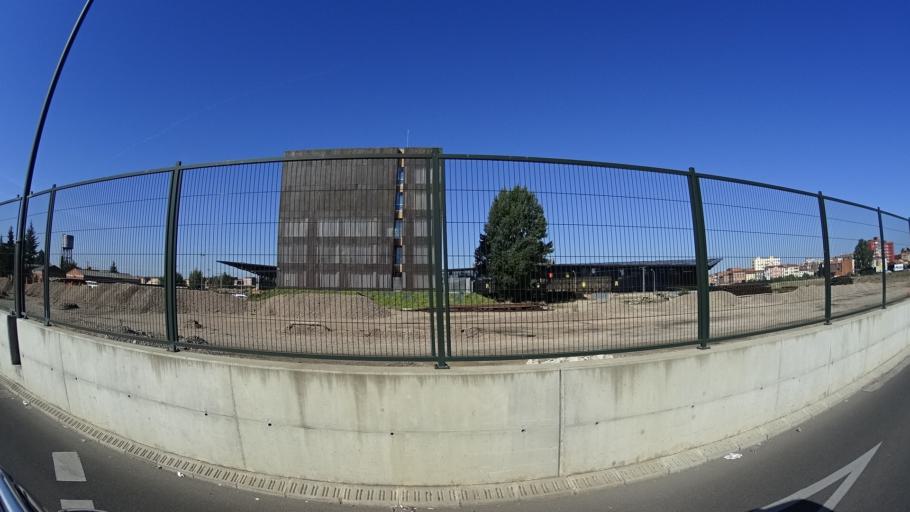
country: ES
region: Castille and Leon
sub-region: Provincia de Leon
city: Leon
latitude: 42.5942
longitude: -5.5812
